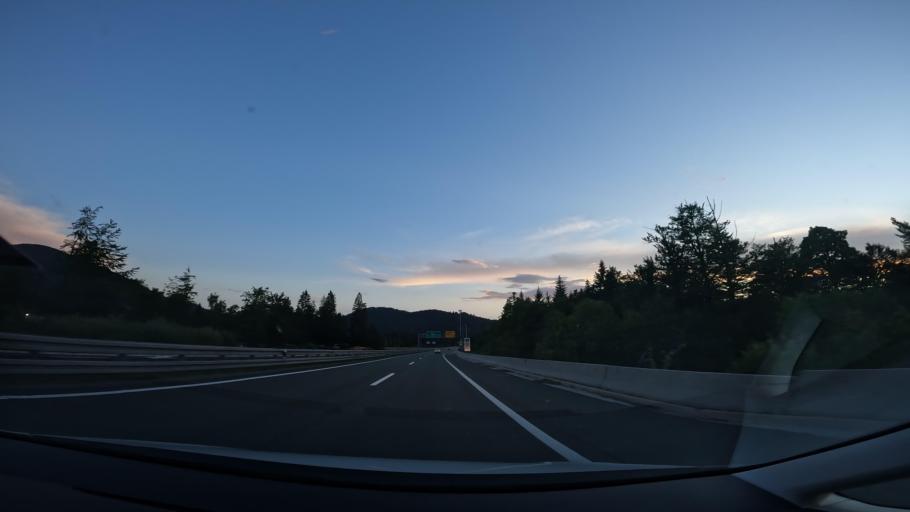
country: HR
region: Primorsko-Goranska
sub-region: Grad Delnice
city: Delnice
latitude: 45.3780
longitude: 14.7967
